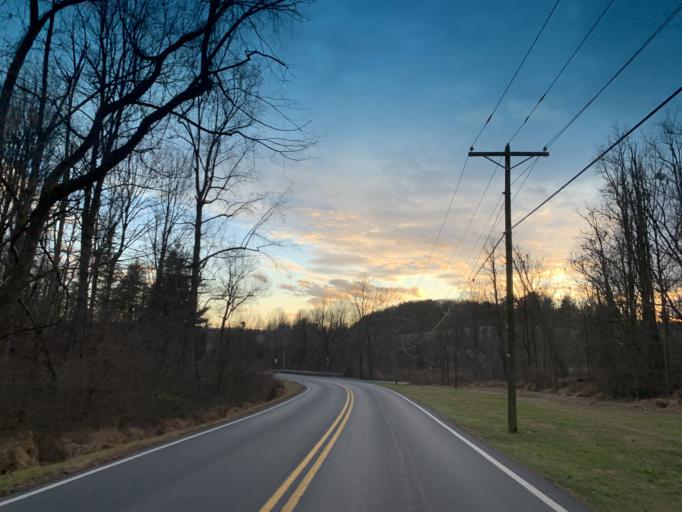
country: US
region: Maryland
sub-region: Harford County
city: Bel Air North
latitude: 39.6380
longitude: -76.3035
